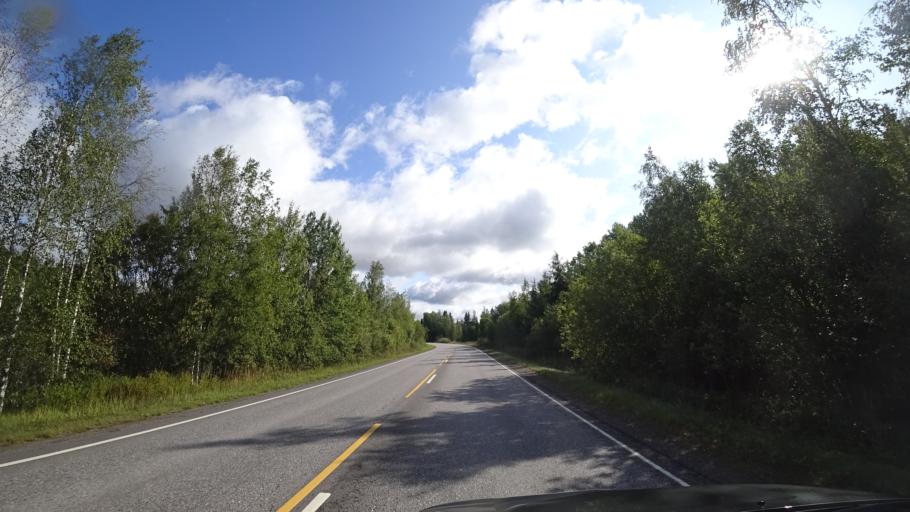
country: FI
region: Uusimaa
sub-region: Helsinki
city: Hyvinge
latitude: 60.5509
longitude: 24.9507
